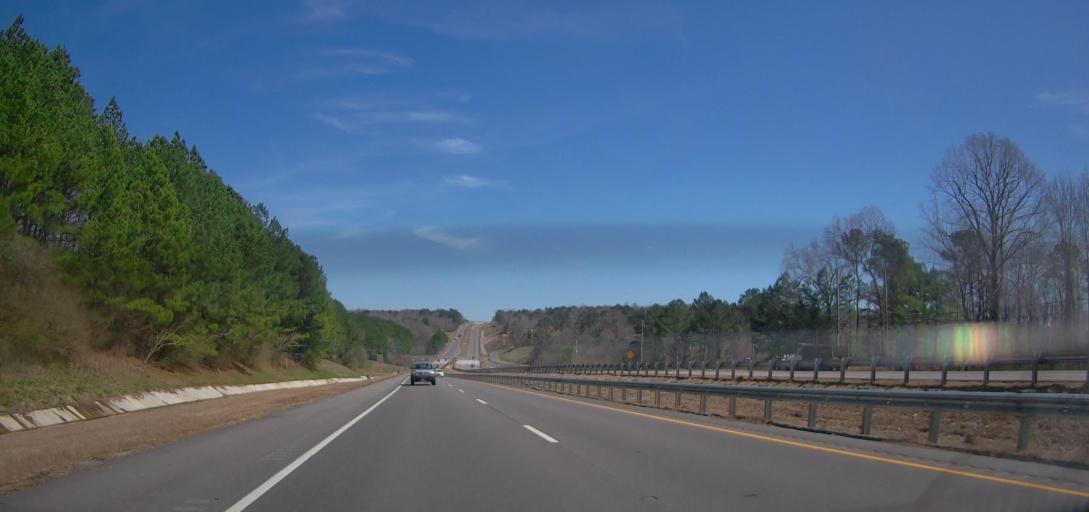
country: US
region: Alabama
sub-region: Cullman County
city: Cullman
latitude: 34.1831
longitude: -86.7783
